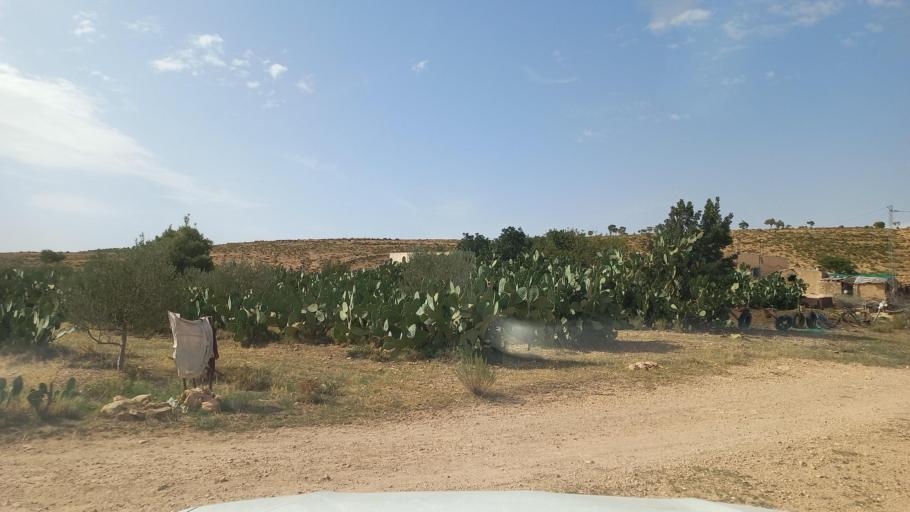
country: TN
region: Al Qasrayn
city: Kasserine
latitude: 35.3694
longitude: 8.8671
